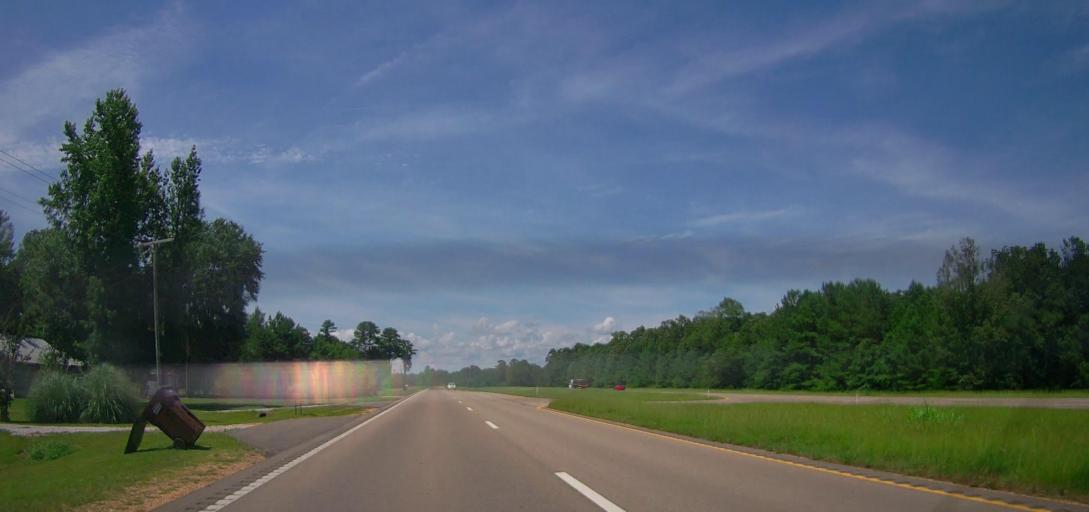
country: US
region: Mississippi
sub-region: Monroe County
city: Amory
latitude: 33.9347
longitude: -88.5971
